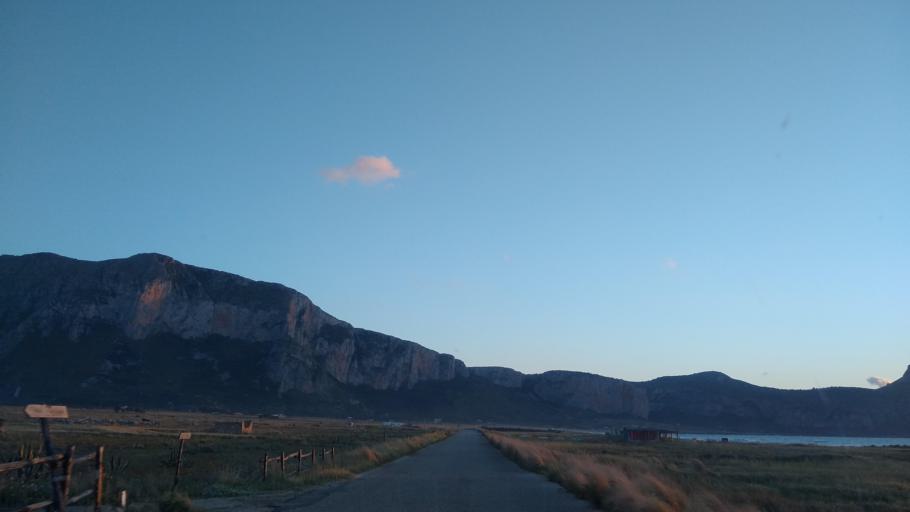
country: IT
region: Sicily
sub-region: Trapani
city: Castelluzzo
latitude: 38.1209
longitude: 12.7241
